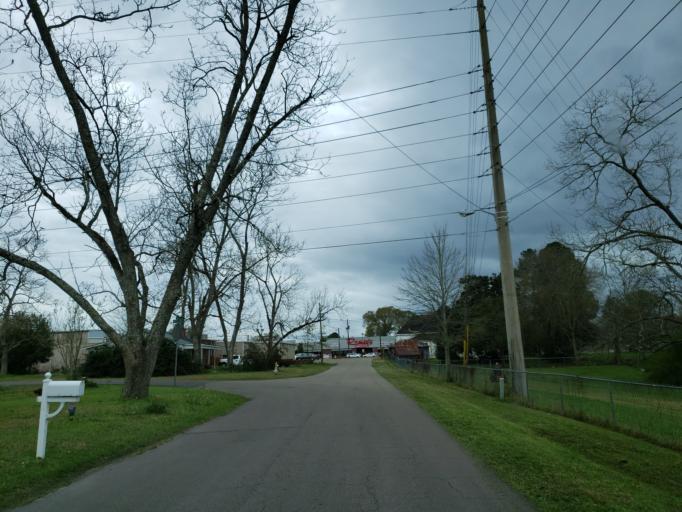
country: US
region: Mississippi
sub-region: Lamar County
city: Purvis
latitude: 31.1446
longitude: -89.4064
